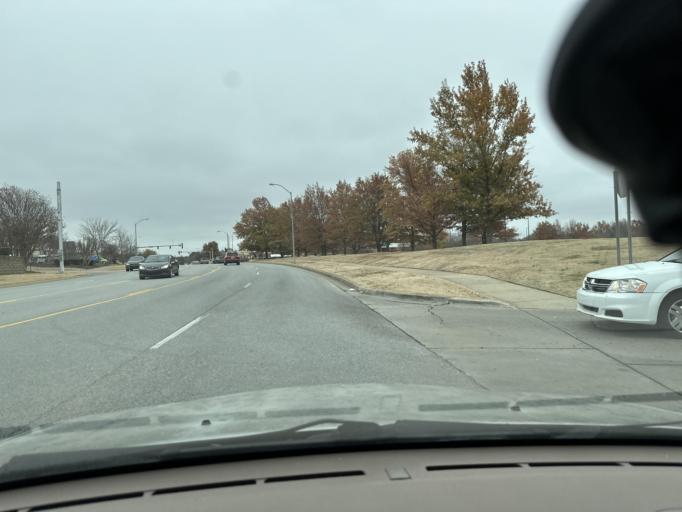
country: US
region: Arkansas
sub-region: Washington County
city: Johnson
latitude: 36.1238
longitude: -94.1519
